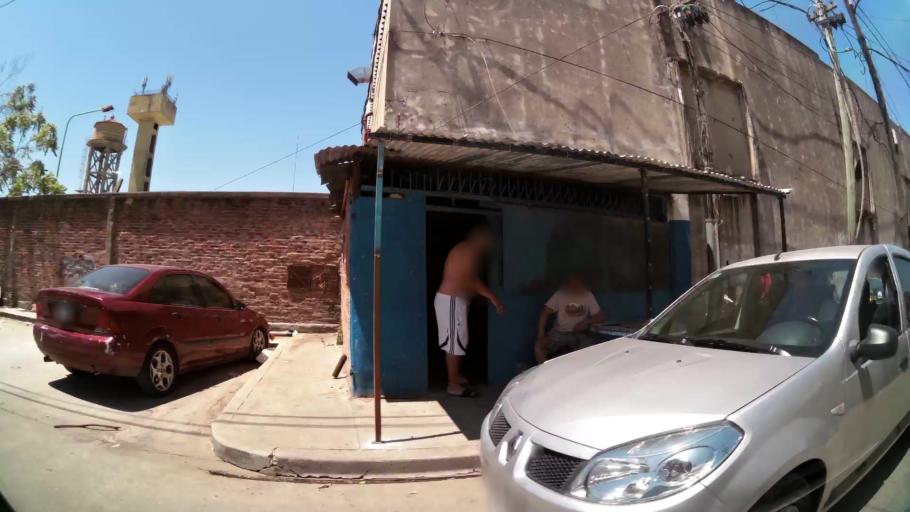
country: AR
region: Buenos Aires
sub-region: Partido de Avellaneda
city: Avellaneda
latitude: -34.6599
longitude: -58.3947
